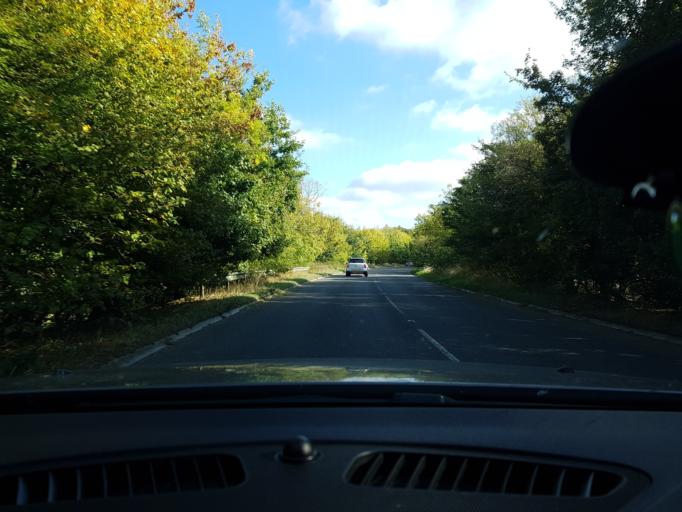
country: GB
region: England
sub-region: Wiltshire
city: Aldbourne
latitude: 51.4955
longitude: -1.5817
